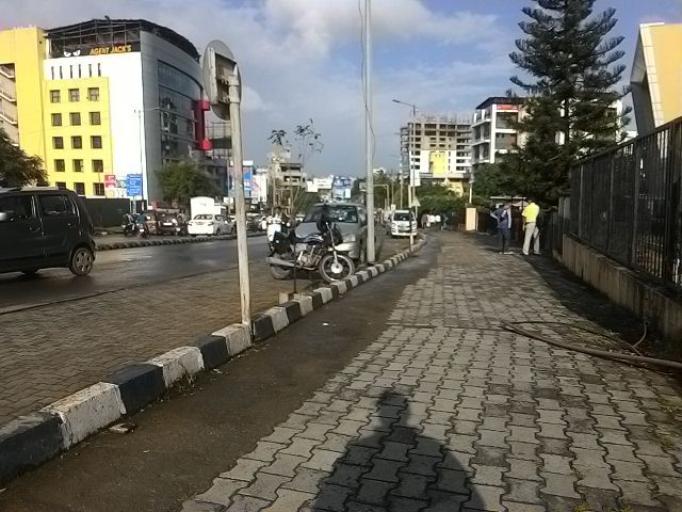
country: IN
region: Maharashtra
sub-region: Pune Division
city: Khadki
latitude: 18.5548
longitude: 73.7964
